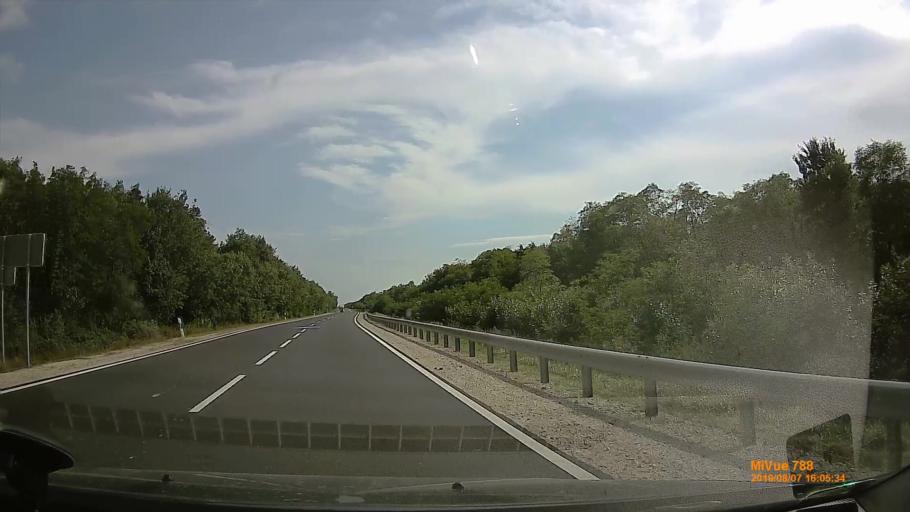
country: HU
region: Vas
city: Kormend
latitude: 46.9524
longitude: 16.6029
